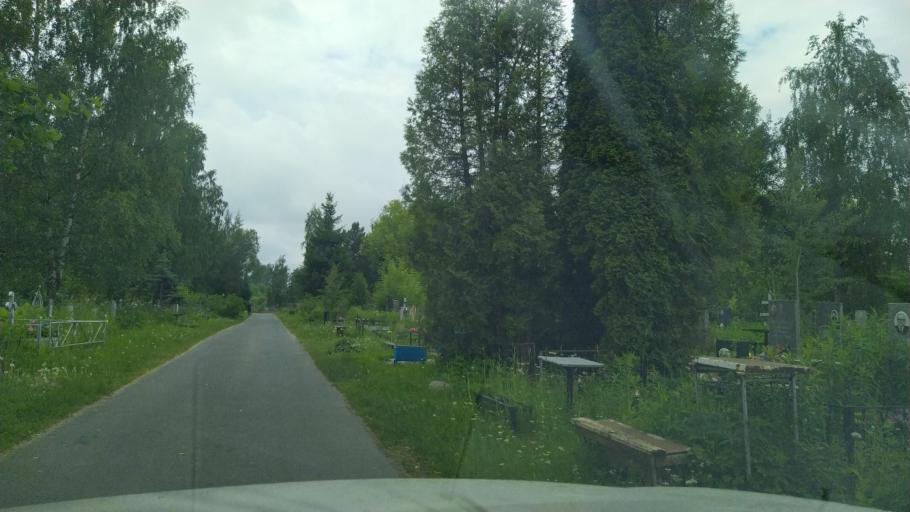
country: RU
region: St.-Petersburg
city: Pushkin
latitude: 59.6930
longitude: 30.3824
